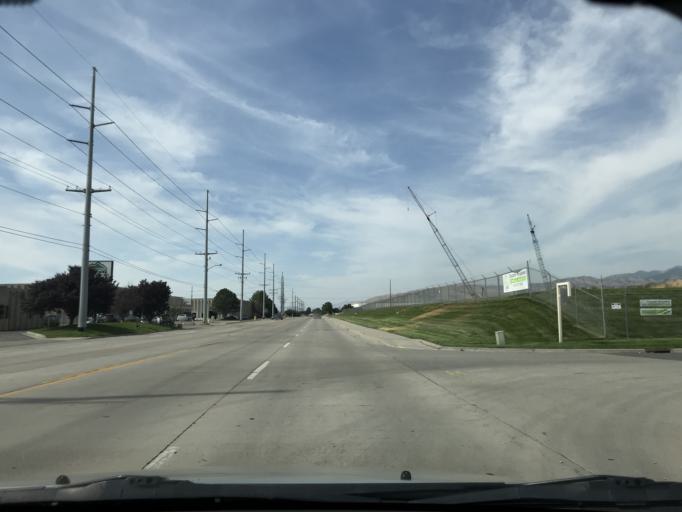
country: US
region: Utah
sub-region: Salt Lake County
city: Centerfield
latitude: 40.7053
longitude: -111.9169
